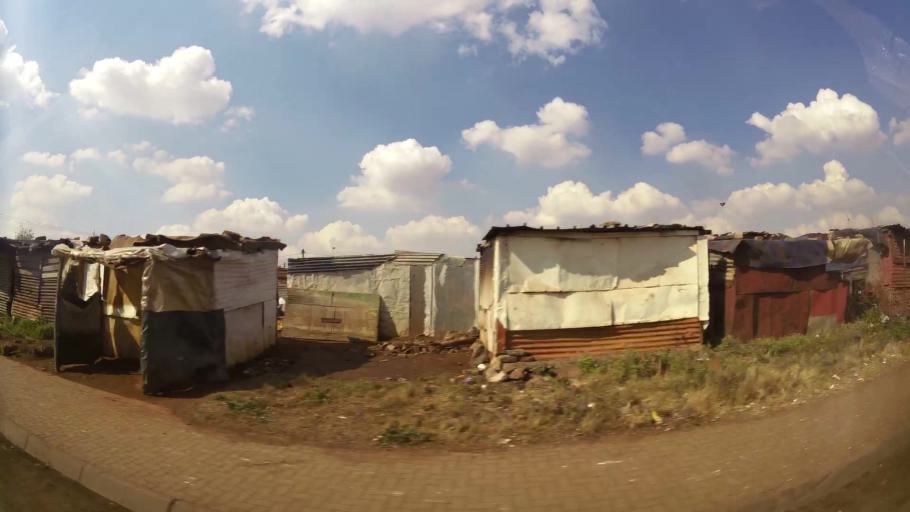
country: ZA
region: Gauteng
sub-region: Ekurhuleni Metropolitan Municipality
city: Germiston
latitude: -26.3197
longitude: 28.1436
